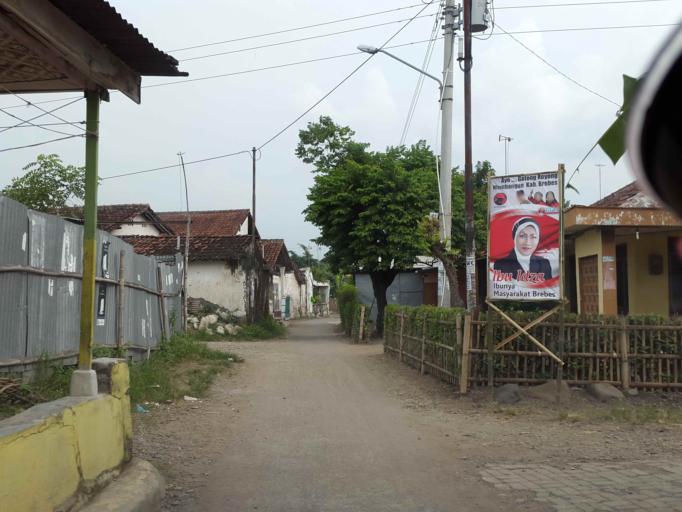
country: ID
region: Central Java
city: Dukuhturi
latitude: -6.9676
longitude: 109.0554
